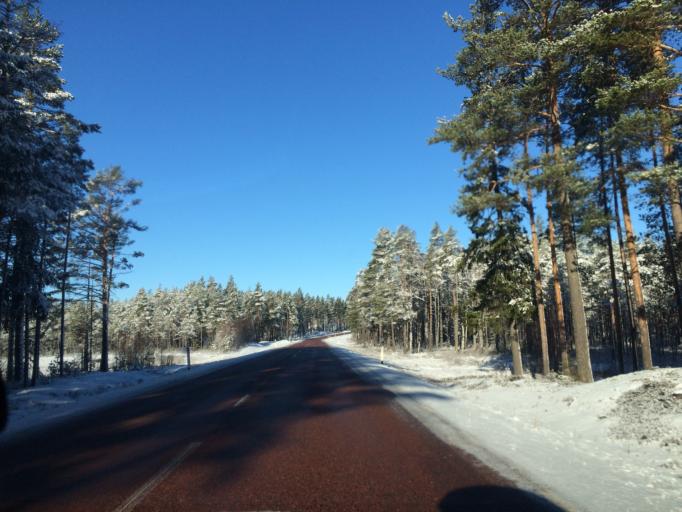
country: SE
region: Dalarna
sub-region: Mora Kommun
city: Mora
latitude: 60.8478
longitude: 14.2675
